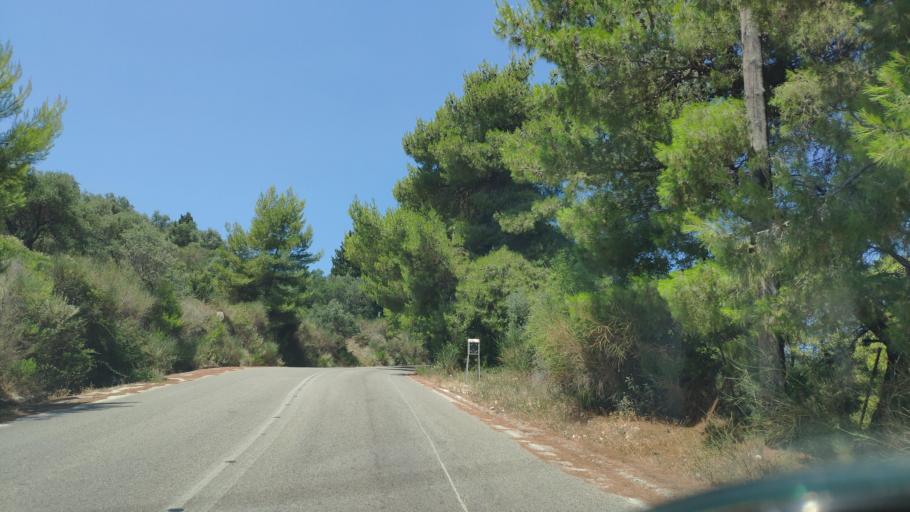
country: GR
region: Ionian Islands
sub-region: Lefkada
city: Lefkada
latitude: 38.8026
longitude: 20.6905
